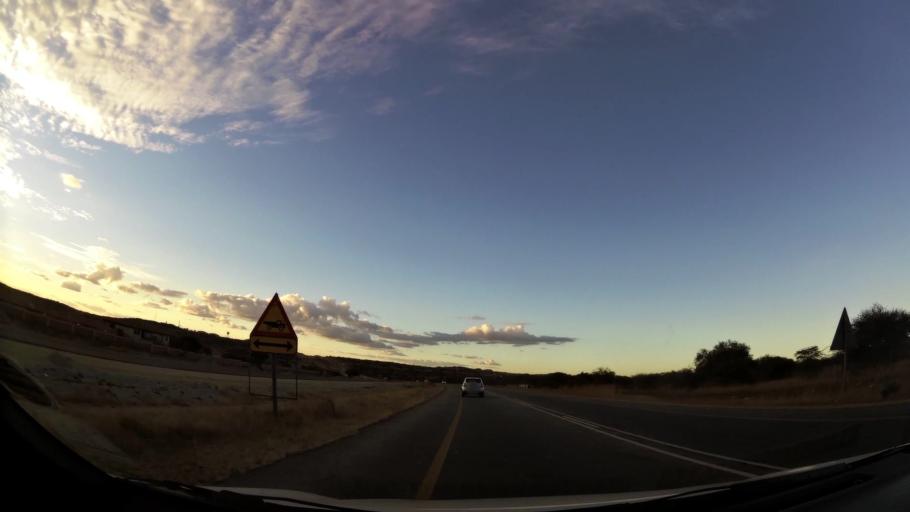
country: ZA
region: Limpopo
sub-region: Capricorn District Municipality
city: Polokwane
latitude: -23.9100
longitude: 29.5097
